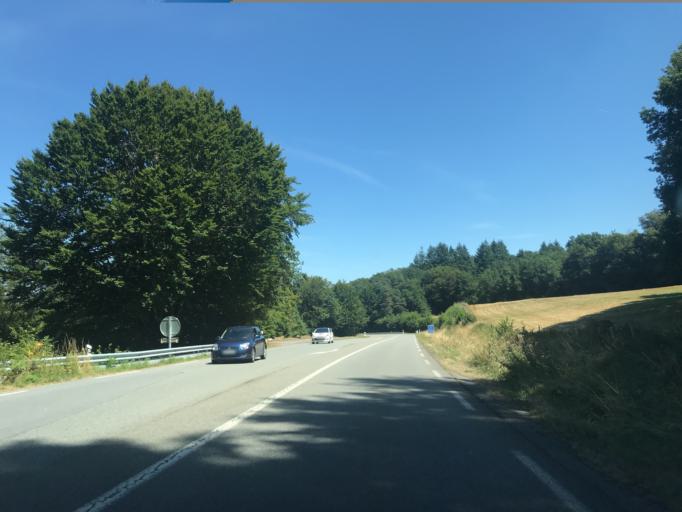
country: FR
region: Limousin
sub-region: Departement de la Correze
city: Egletons
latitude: 45.4105
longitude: 2.0522
